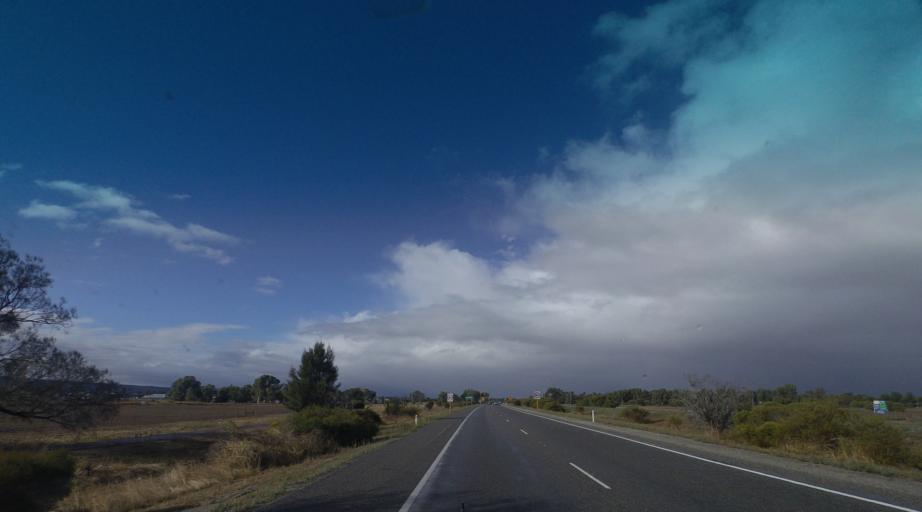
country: AU
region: Western Australia
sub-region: Serpentine-Jarrahdale
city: Oakford
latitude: -32.1763
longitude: 115.9617
